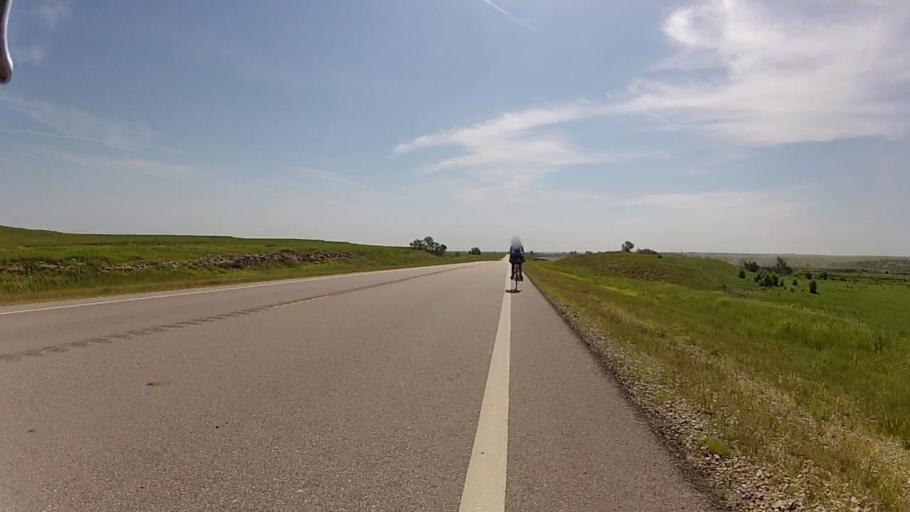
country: US
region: Kansas
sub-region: Cowley County
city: Winfield
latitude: 37.1108
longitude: -96.6284
